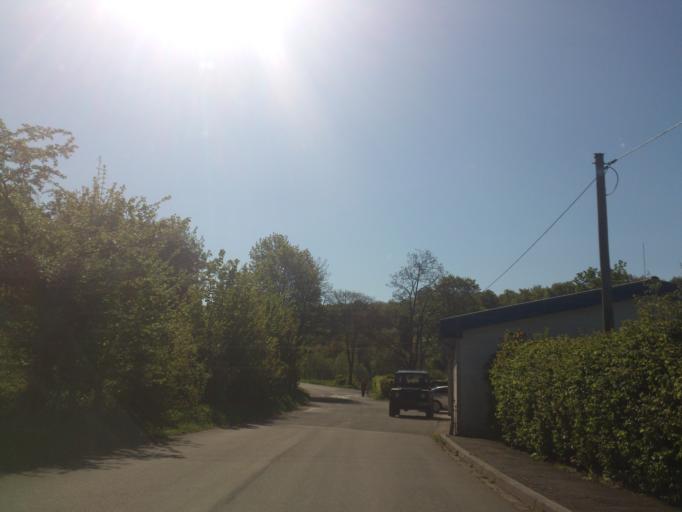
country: DE
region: North Rhine-Westphalia
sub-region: Regierungsbezirk Detmold
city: Willebadessen
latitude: 51.6701
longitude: 8.9933
